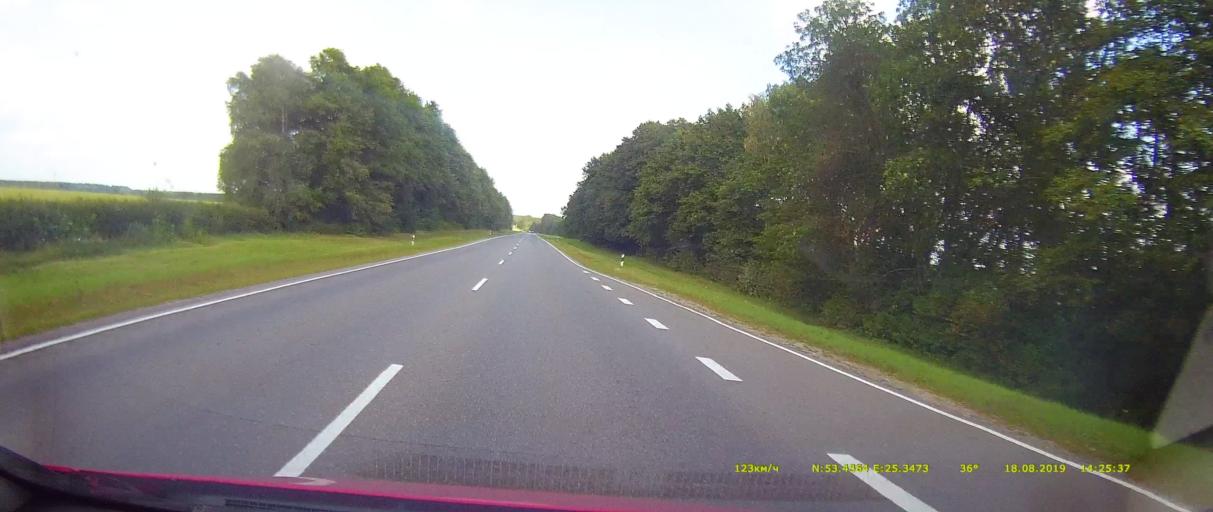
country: BY
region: Grodnenskaya
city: Dzyatlava
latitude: 53.4510
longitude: 25.3628
